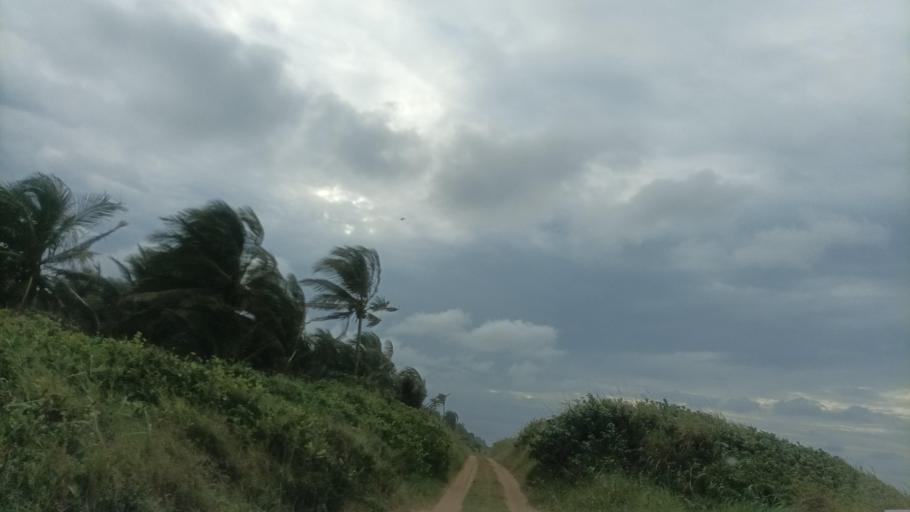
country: MX
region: Veracruz
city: Agua Dulce
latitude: 18.1830
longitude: -94.2594
